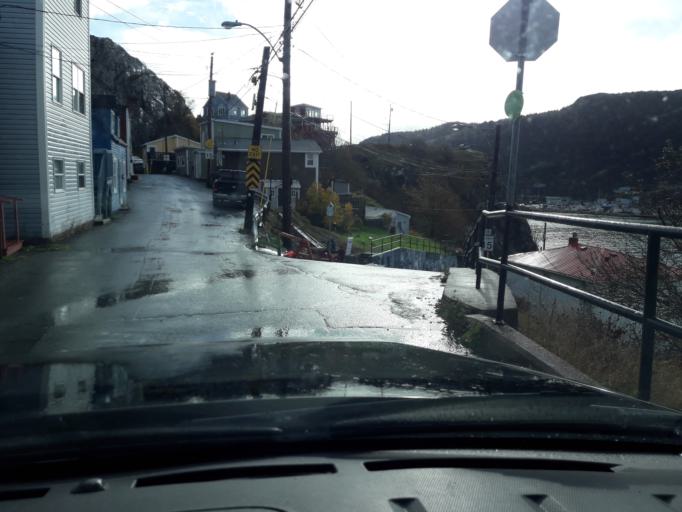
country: CA
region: Newfoundland and Labrador
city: St. John's
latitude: 47.5700
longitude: -52.6918
